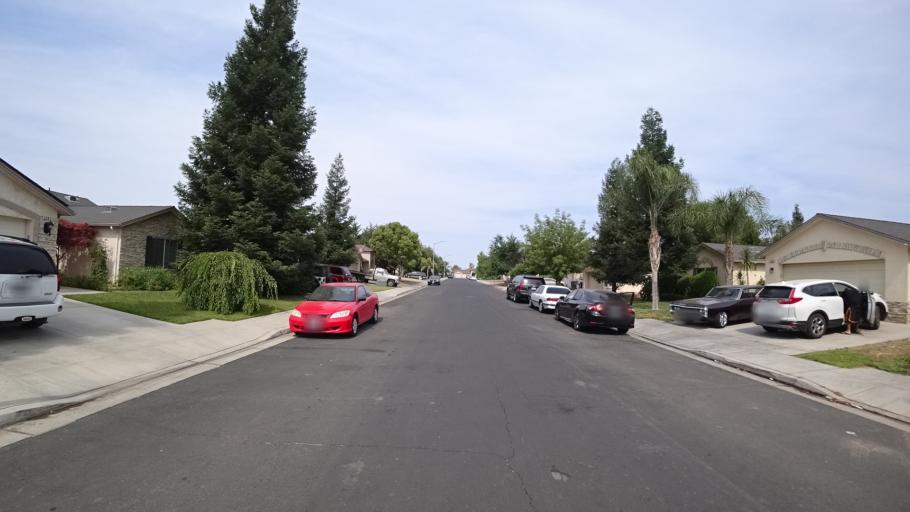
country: US
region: California
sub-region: Fresno County
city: West Park
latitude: 36.7591
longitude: -119.8913
